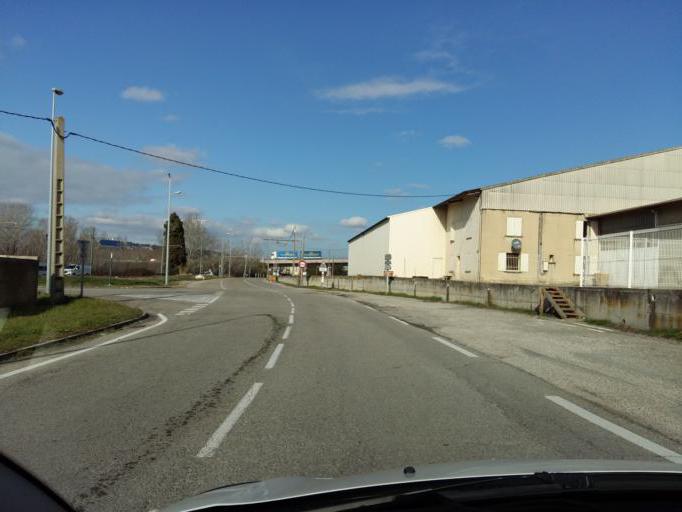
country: FR
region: Provence-Alpes-Cote d'Azur
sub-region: Departement du Vaucluse
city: Cheval-Blanc
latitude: 43.8159
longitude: 5.0484
